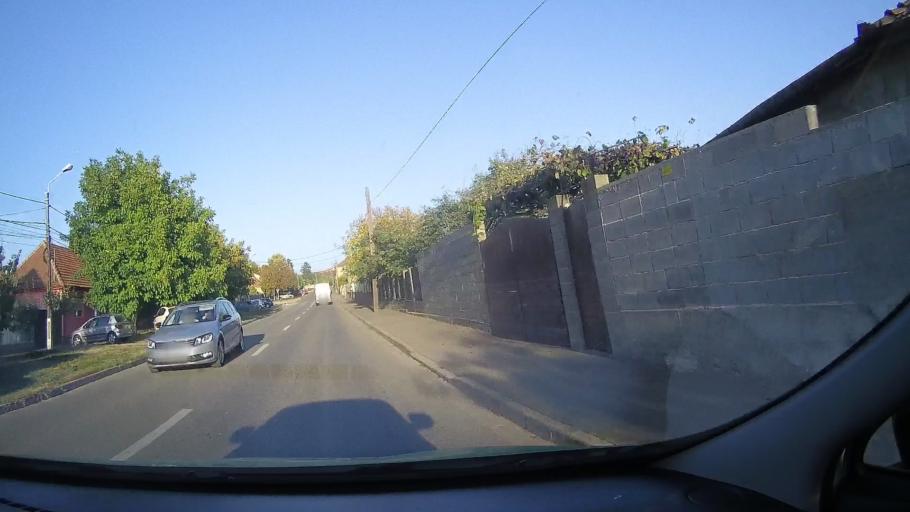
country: RO
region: Bihor
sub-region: Comuna Biharea
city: Oradea
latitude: 47.0882
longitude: 21.9234
